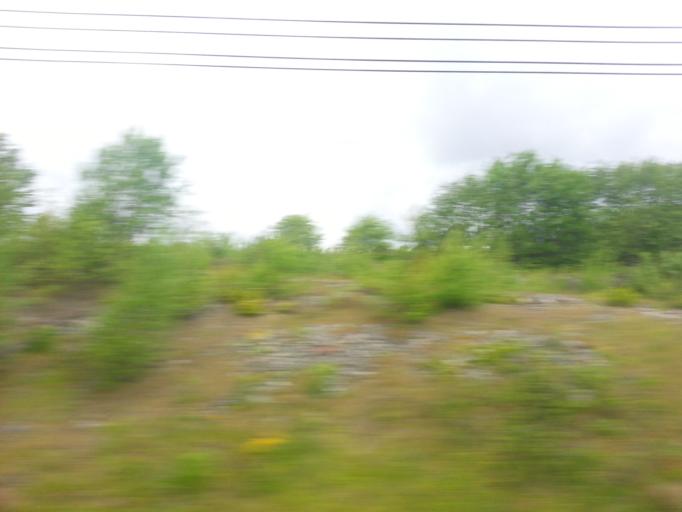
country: NO
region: Akershus
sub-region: Skedsmo
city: Leirsund
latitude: 59.9856
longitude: 11.0763
